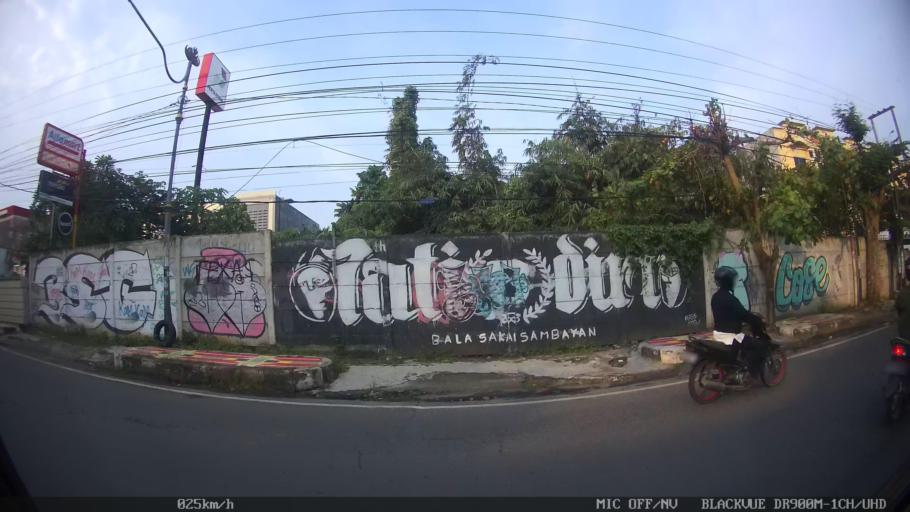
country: ID
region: Lampung
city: Bandarlampung
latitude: -5.4366
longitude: 105.2653
